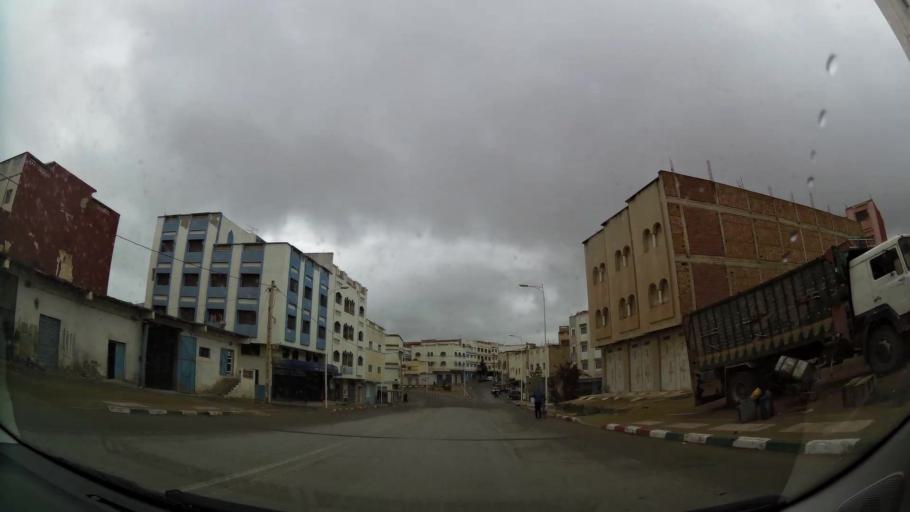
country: MA
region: Oriental
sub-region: Nador
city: Midar
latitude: 35.0478
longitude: -3.4517
